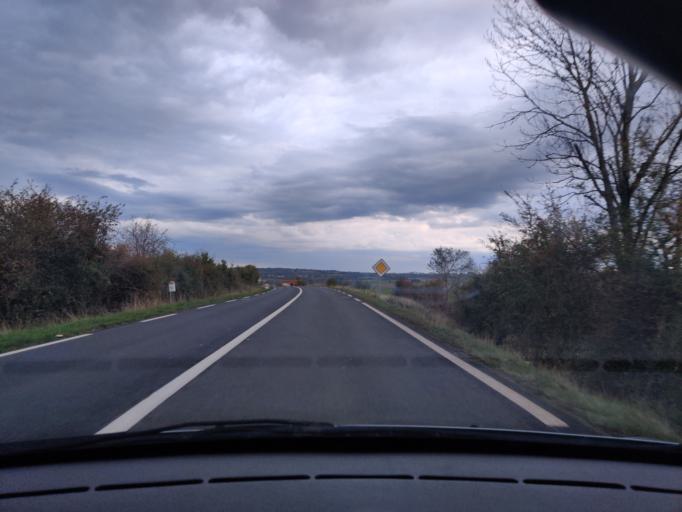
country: FR
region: Auvergne
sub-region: Departement du Puy-de-Dome
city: Combronde
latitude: 45.9988
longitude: 3.0929
